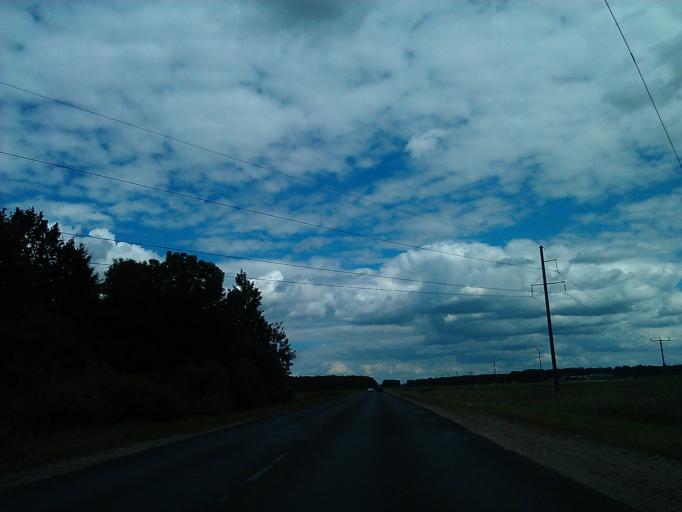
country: LV
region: Jelgava
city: Jelgava
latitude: 56.6259
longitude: 23.5530
